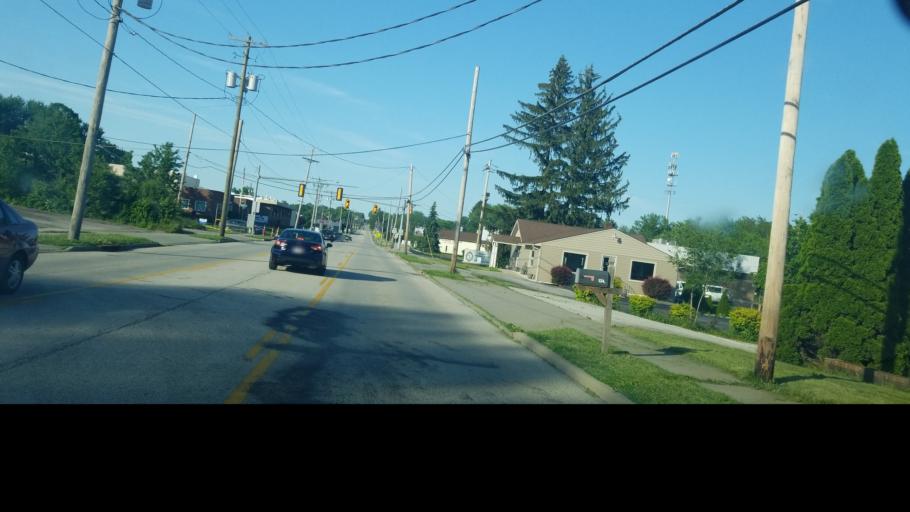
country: US
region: Ohio
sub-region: Summit County
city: Tallmadge
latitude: 41.1043
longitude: -81.4364
